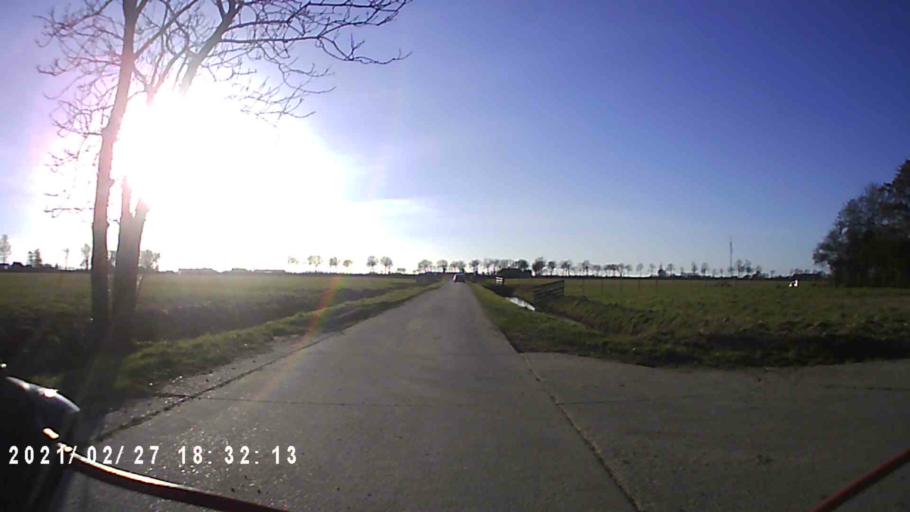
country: NL
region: Groningen
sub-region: Gemeente Winsum
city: Winsum
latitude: 53.3126
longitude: 6.5346
